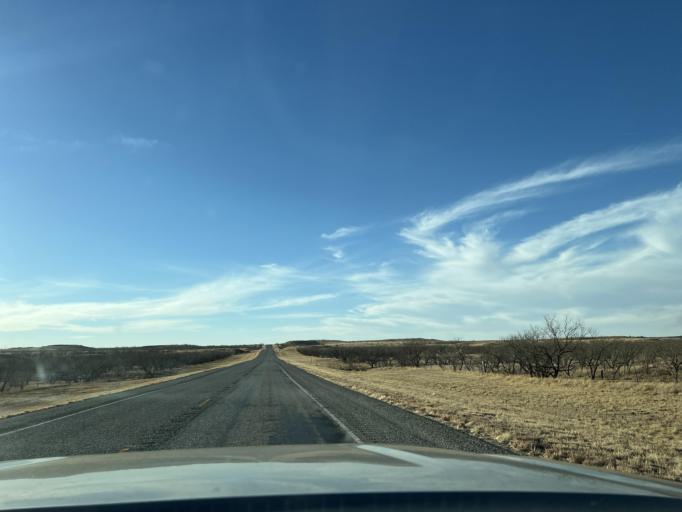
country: US
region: Texas
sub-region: Borden County
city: Gail
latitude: 32.7567
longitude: -101.2472
